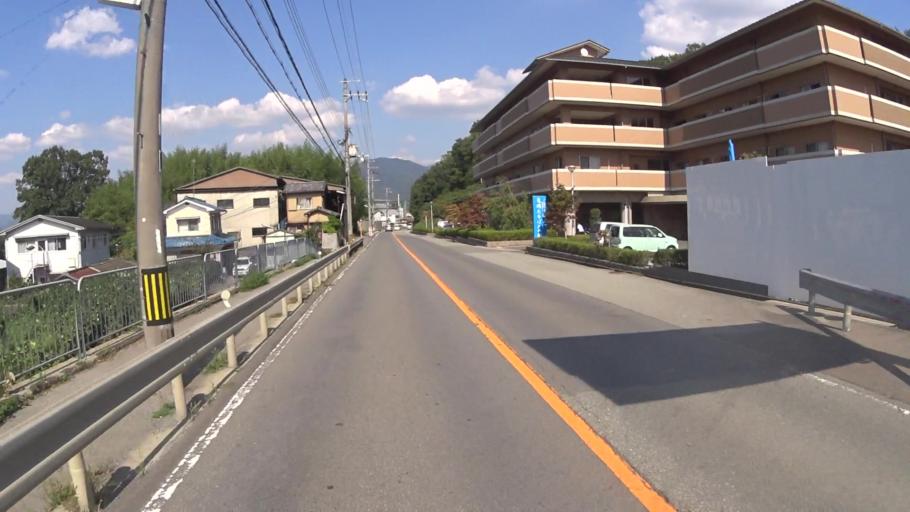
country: JP
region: Kyoto
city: Kameoka
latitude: 35.0111
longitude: 135.5637
